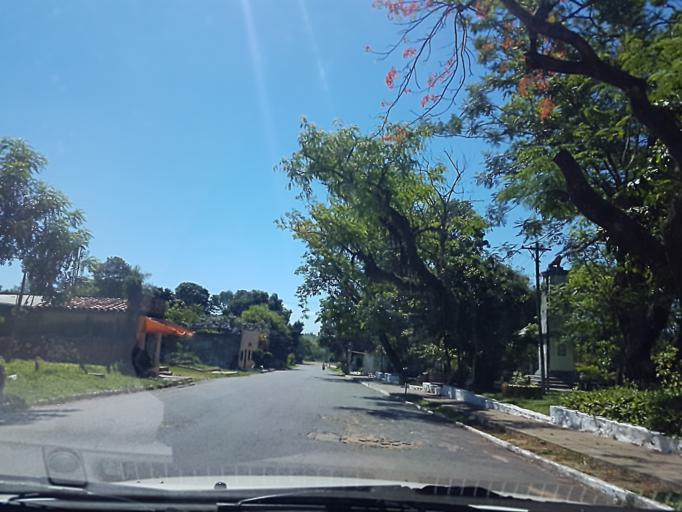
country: PY
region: Cordillera
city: Atyra
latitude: -25.2774
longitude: -57.1717
